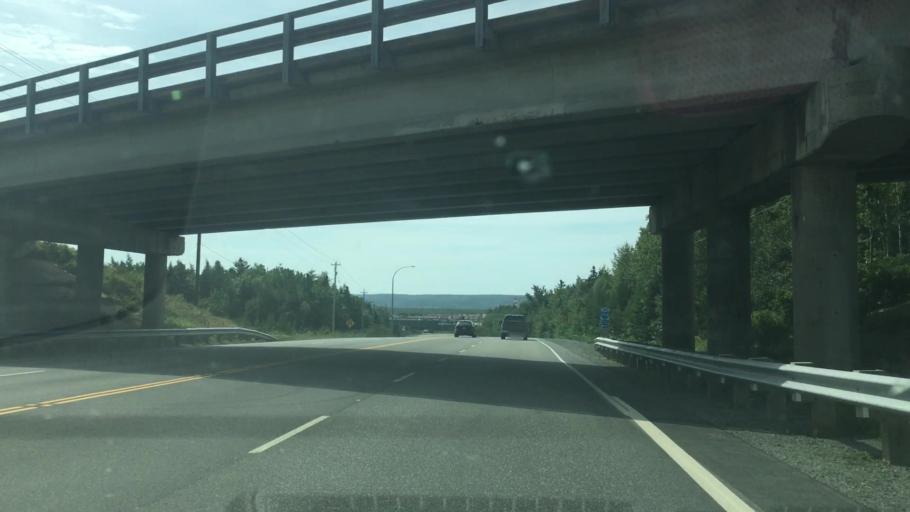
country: CA
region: Nova Scotia
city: Port Hawkesbury
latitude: 45.6252
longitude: -61.3326
